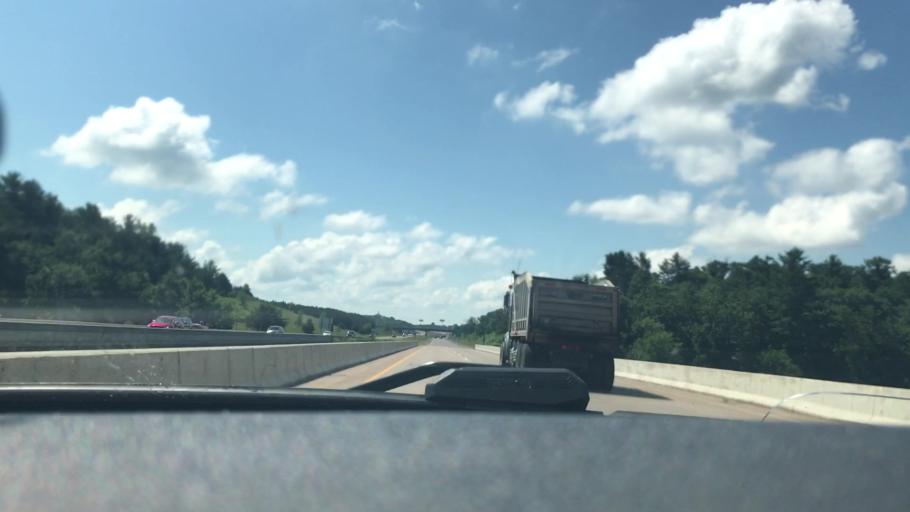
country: US
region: Wisconsin
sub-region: Chippewa County
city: Chippewa Falls
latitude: 44.9223
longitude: -91.4283
